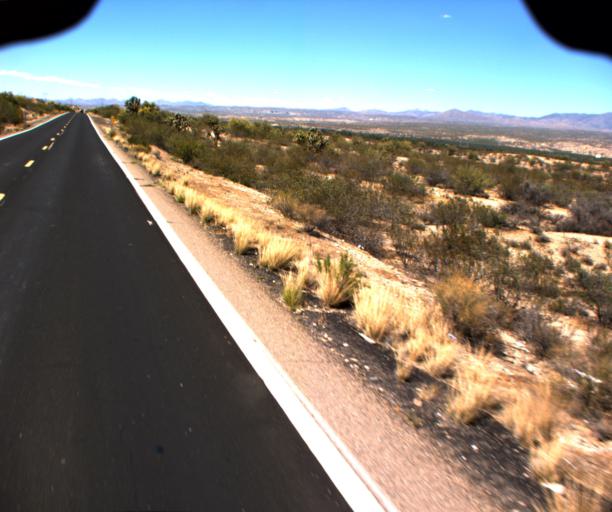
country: US
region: Arizona
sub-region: Yavapai County
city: Bagdad
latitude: 34.7295
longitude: -113.6151
